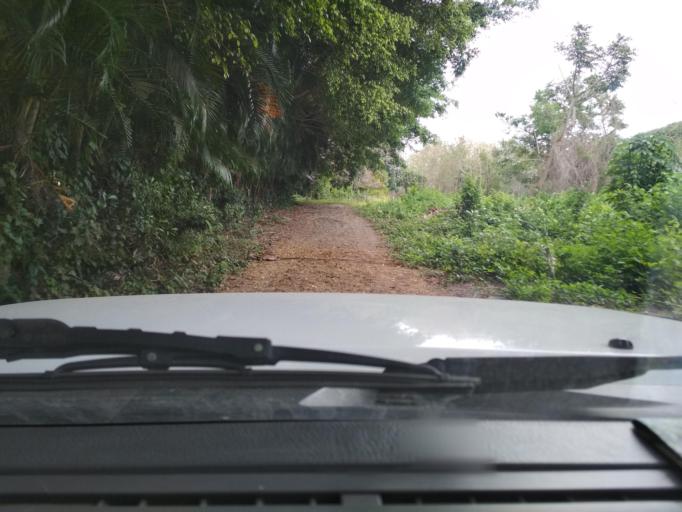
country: MX
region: Veracruz
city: Paso del Toro
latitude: 19.0560
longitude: -96.1353
